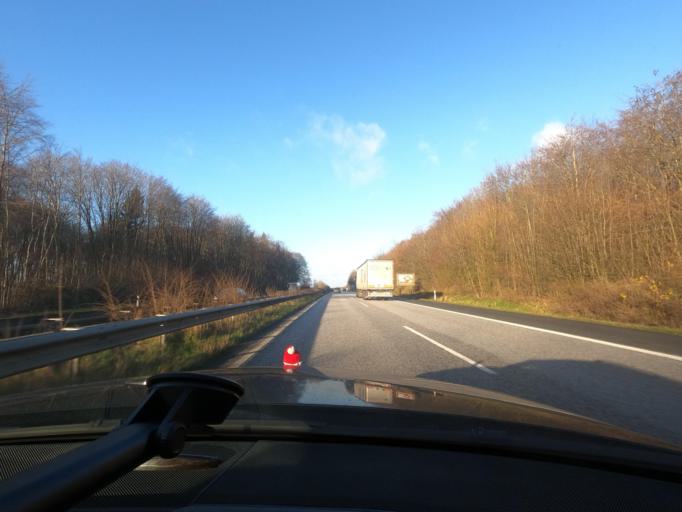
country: DE
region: Schleswig-Holstein
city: Schuby
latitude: 54.5129
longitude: 9.4973
